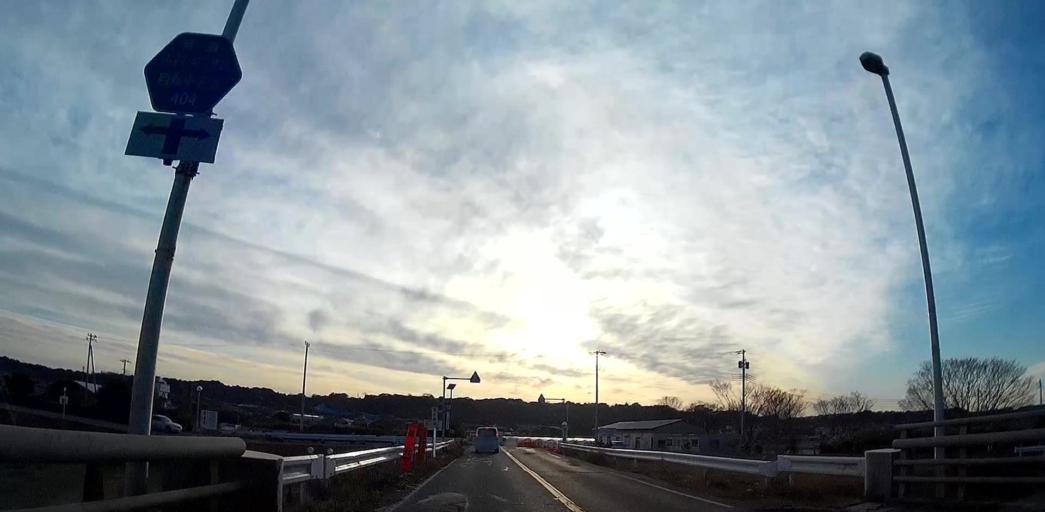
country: JP
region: Chiba
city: Omigawa
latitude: 35.8338
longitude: 140.6994
